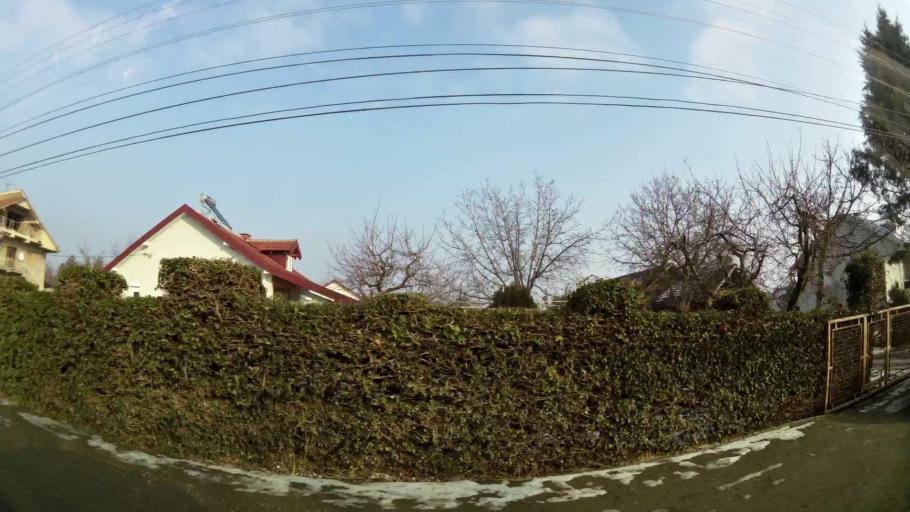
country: MK
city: Kadino
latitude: 41.9696
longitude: 21.5963
